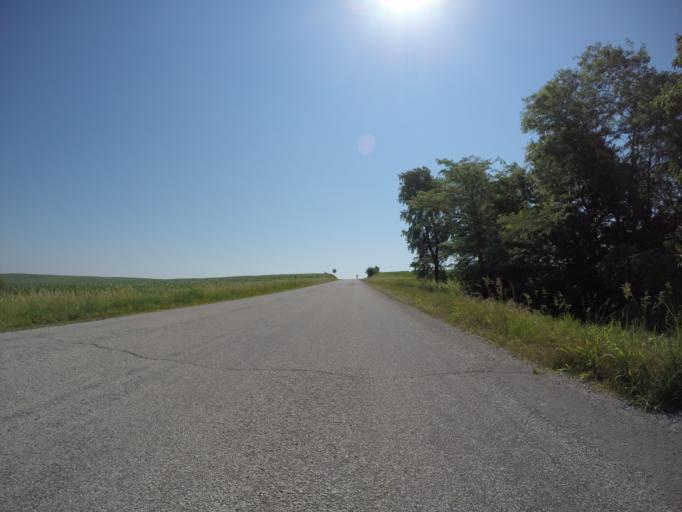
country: US
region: Kansas
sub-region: Doniphan County
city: Highland
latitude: 39.8565
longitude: -95.3709
